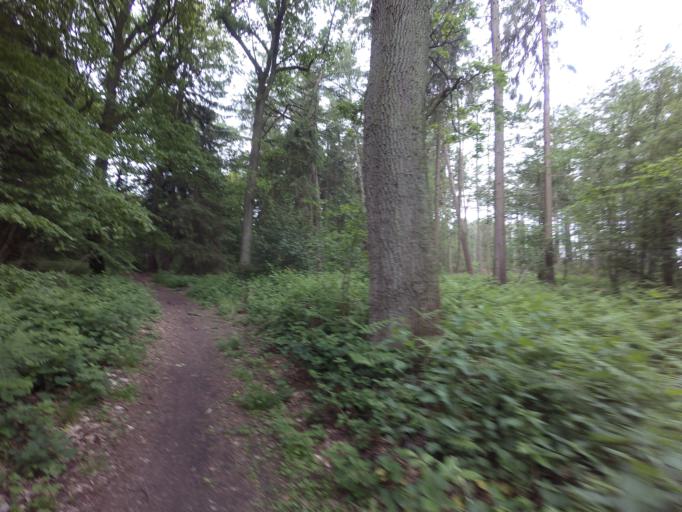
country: BE
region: Wallonia
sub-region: Province de Liege
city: Aubel
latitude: 50.7618
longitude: 5.8912
